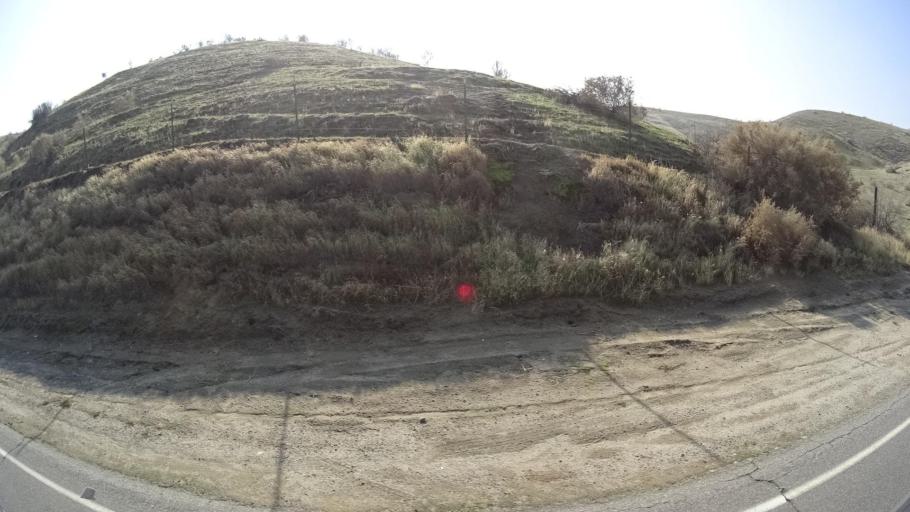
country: US
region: California
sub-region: Kern County
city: Buttonwillow
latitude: 35.2886
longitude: -119.3401
